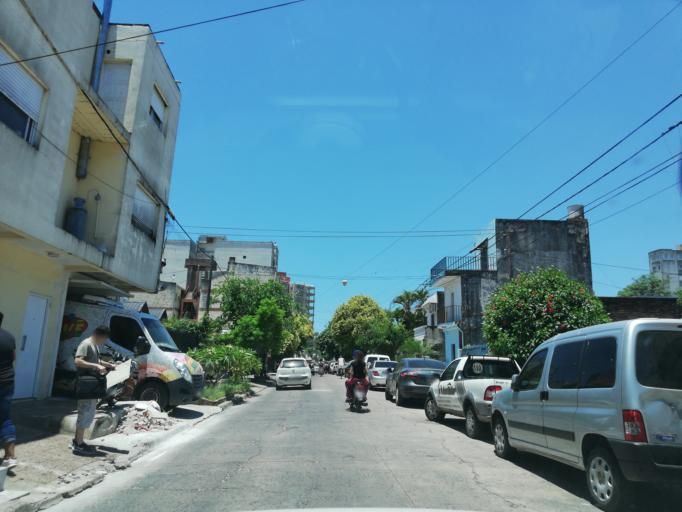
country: AR
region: Corrientes
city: Corrientes
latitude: -27.4650
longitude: -58.8260
